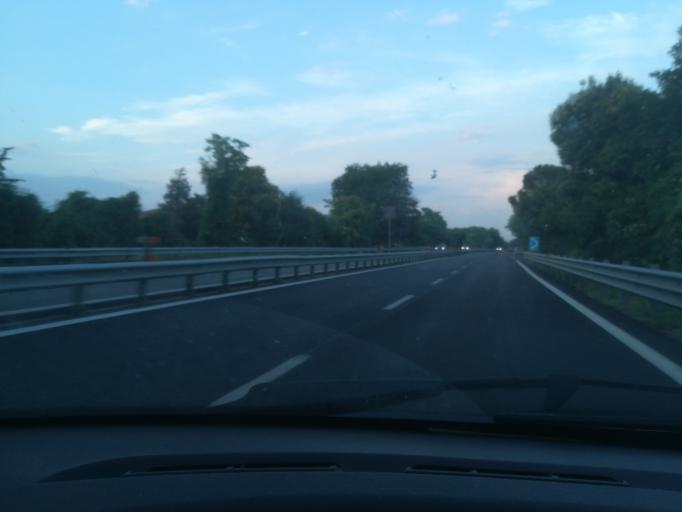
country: IT
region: The Marches
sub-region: Provincia di Macerata
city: Sforzacosta
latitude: 43.2552
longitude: 13.4500
